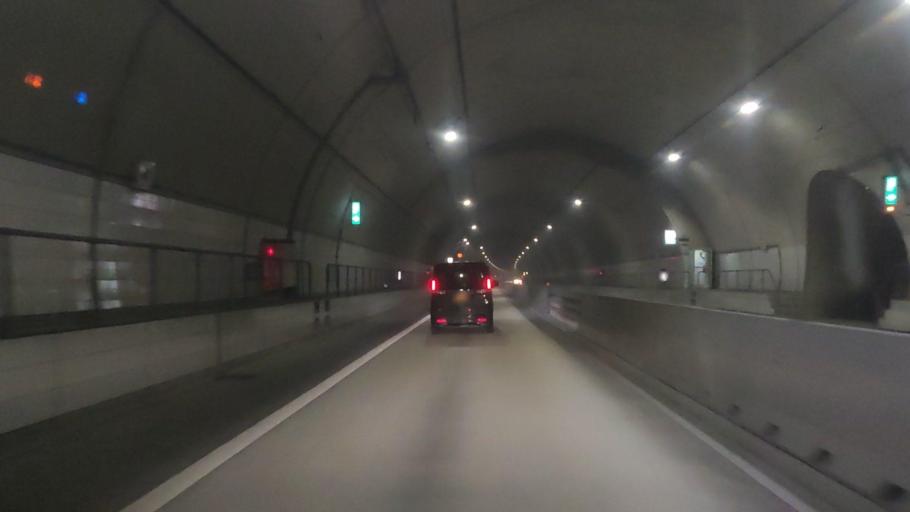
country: JP
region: Kumamoto
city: Ozu
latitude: 32.9063
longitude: 130.9592
